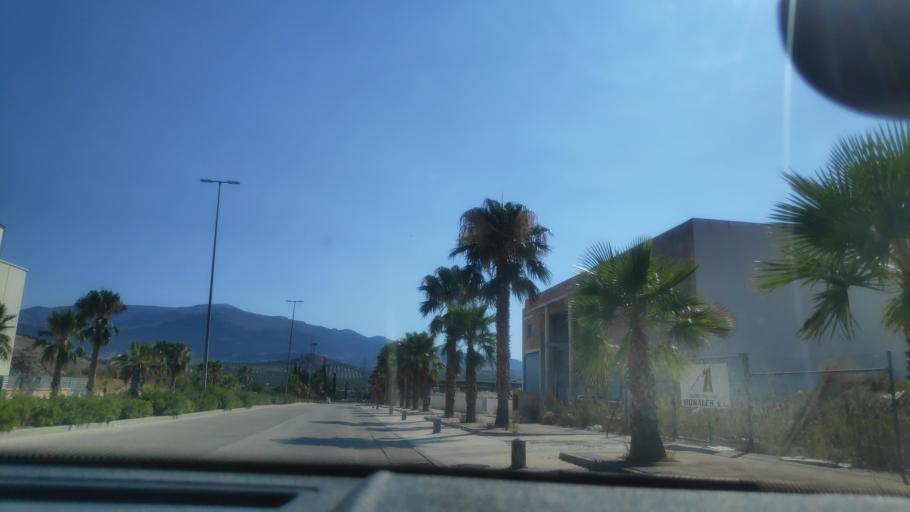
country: ES
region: Andalusia
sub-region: Provincia de Jaen
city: Jaen
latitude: 37.8155
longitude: -3.7833
